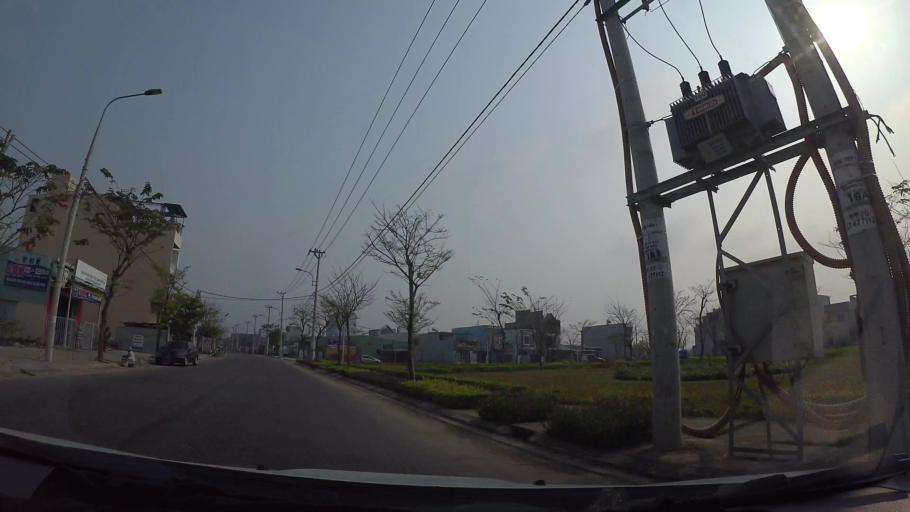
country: VN
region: Da Nang
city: Ngu Hanh Son
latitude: 16.0077
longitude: 108.2286
